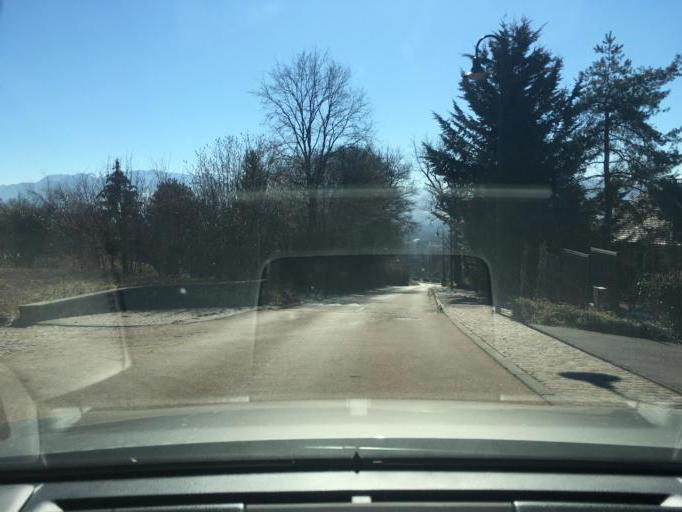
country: FR
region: Rhone-Alpes
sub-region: Departement de la Haute-Savoie
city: Vetraz-Monthoux
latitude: 46.1811
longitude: 6.2585
